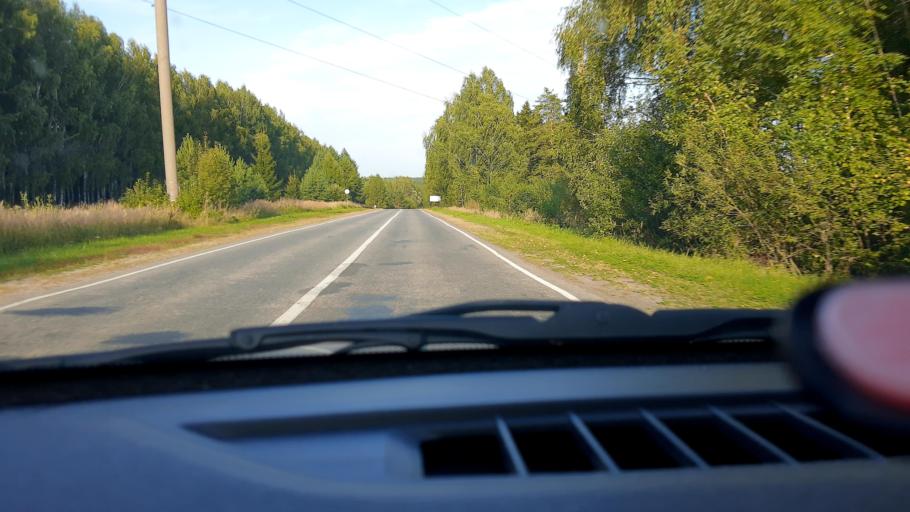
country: RU
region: Nizjnij Novgorod
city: Gorodets
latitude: 56.6631
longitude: 43.5531
